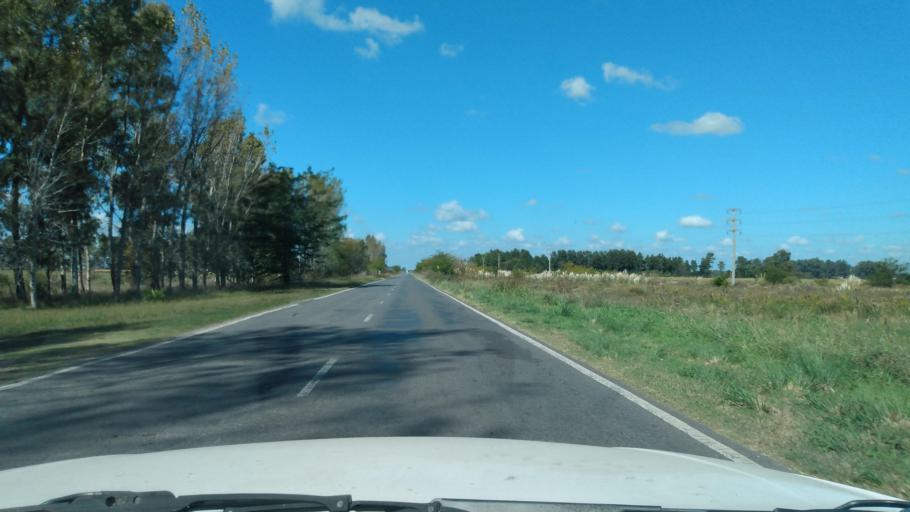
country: AR
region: Buenos Aires
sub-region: Partido de Mercedes
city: Mercedes
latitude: -34.7154
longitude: -59.3971
